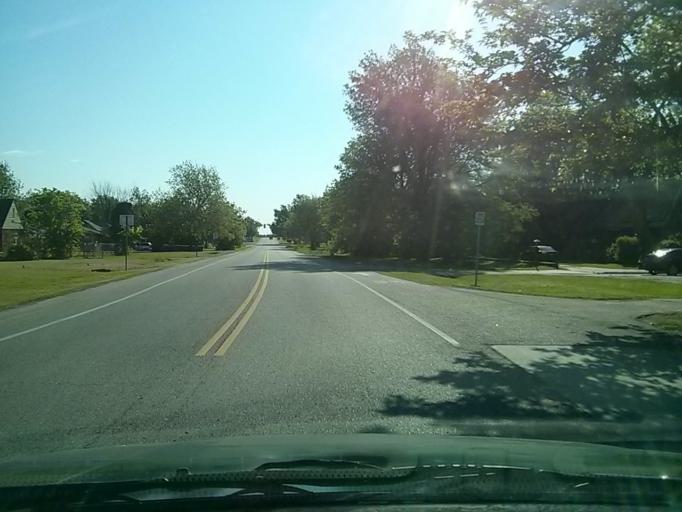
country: US
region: Oklahoma
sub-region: Tulsa County
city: Tulsa
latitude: 36.1926
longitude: -95.9890
